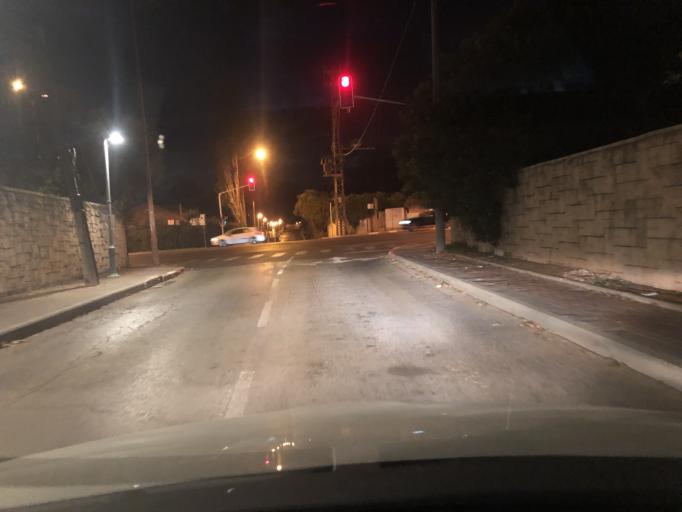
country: IL
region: Central District
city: Hod HaSharon
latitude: 32.1679
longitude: 34.8941
